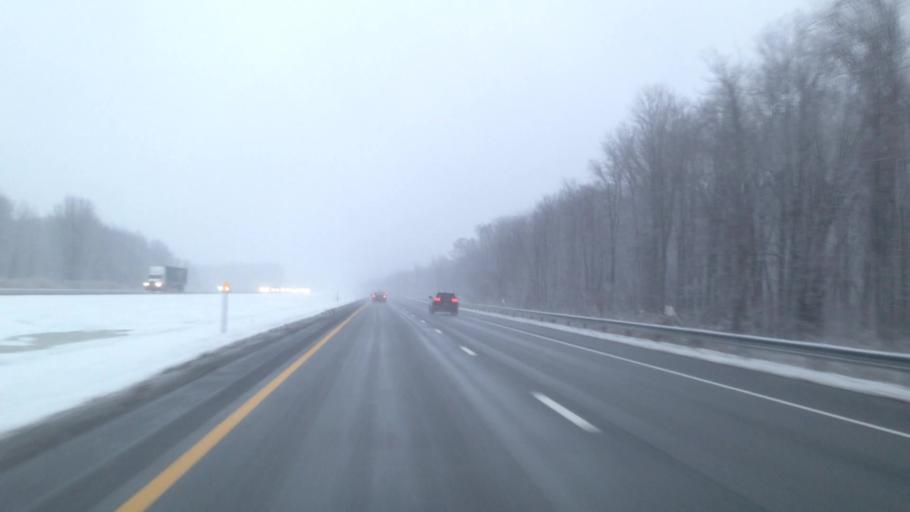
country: US
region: New York
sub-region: Madison County
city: Bolivar
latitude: 43.0913
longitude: -75.9278
